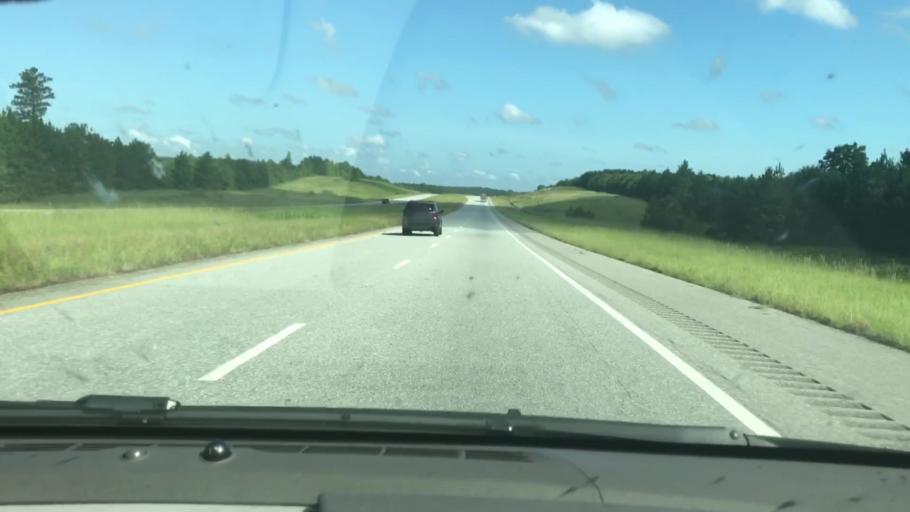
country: US
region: Alabama
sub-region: Barbour County
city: Eufaula
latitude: 32.1722
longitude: -85.1759
